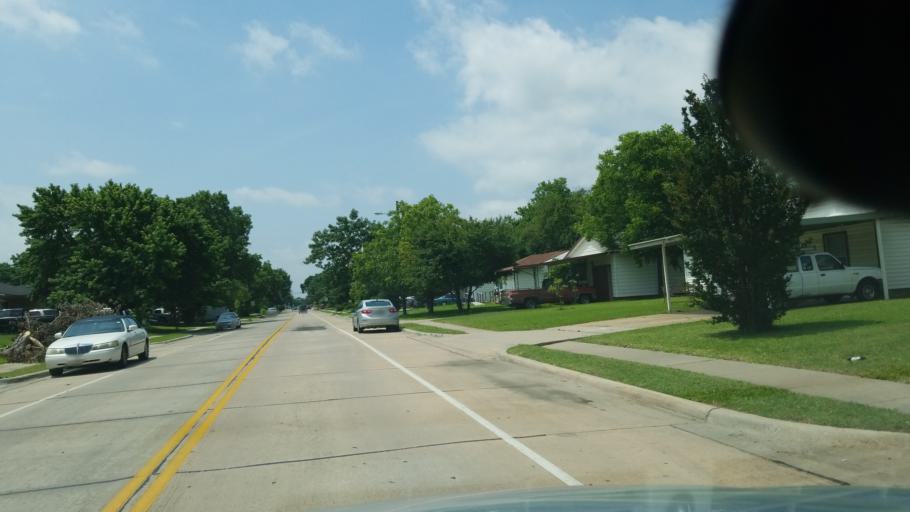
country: US
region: Texas
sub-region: Dallas County
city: Irving
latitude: 32.8332
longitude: -96.9354
